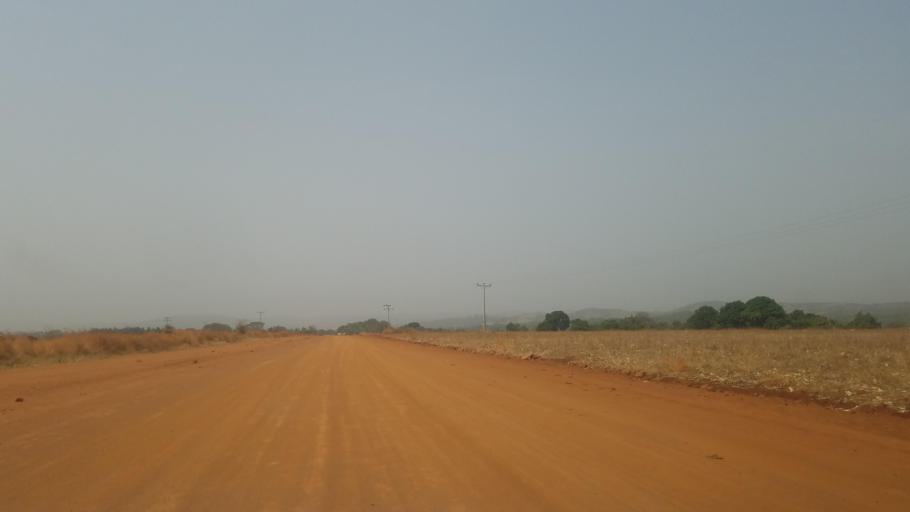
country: ET
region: Amhara
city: Bure
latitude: 10.8945
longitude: 36.4545
